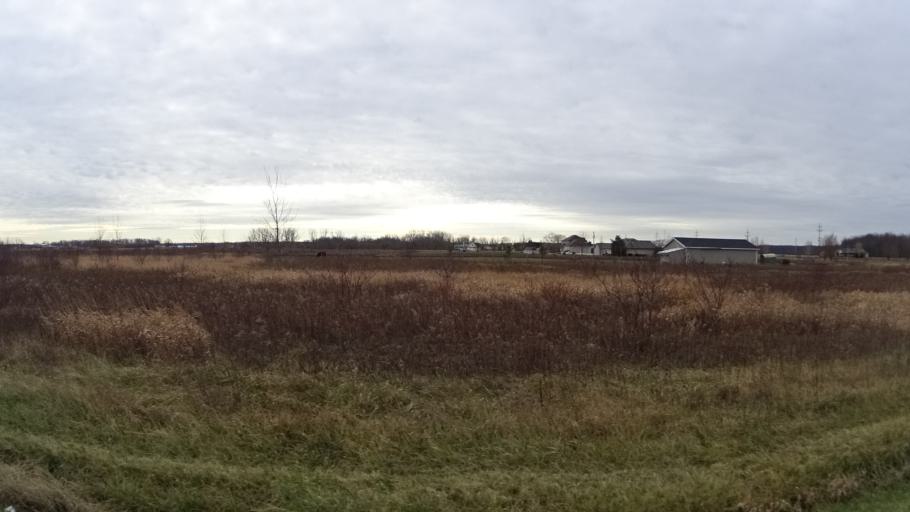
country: US
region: Ohio
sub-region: Lorain County
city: Wellington
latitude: 41.1475
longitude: -82.1798
